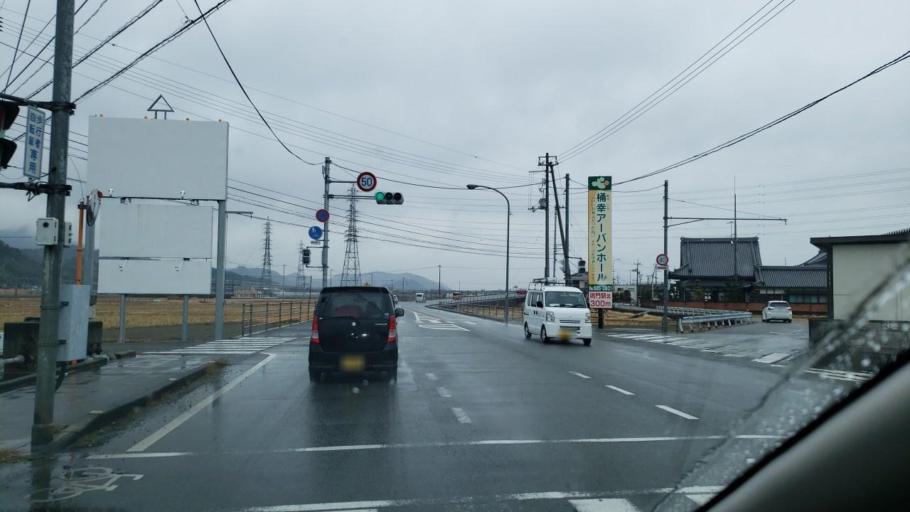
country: JP
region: Tokushima
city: Narutocho-mitsuishi
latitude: 34.1615
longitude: 134.5512
